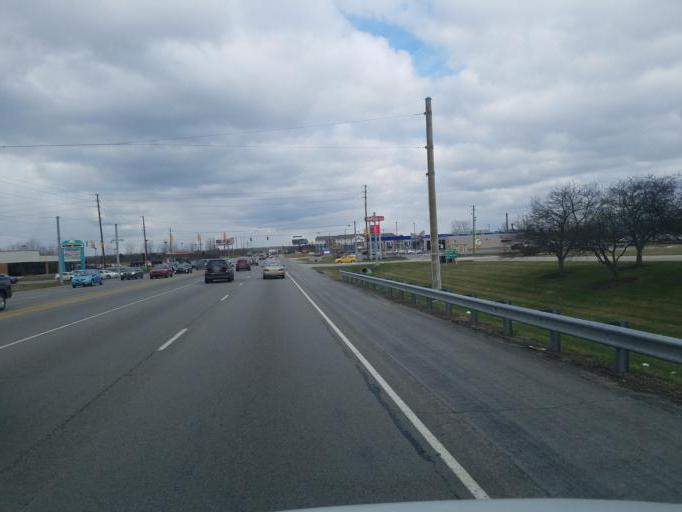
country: US
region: Indiana
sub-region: Marion County
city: Clermont
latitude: 39.7640
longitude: -86.3092
